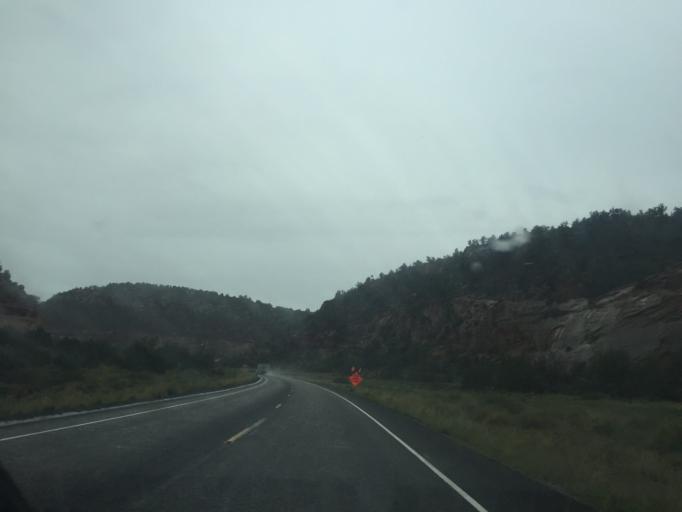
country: US
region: Utah
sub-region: Kane County
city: Kanab
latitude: 37.1188
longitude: -112.5637
